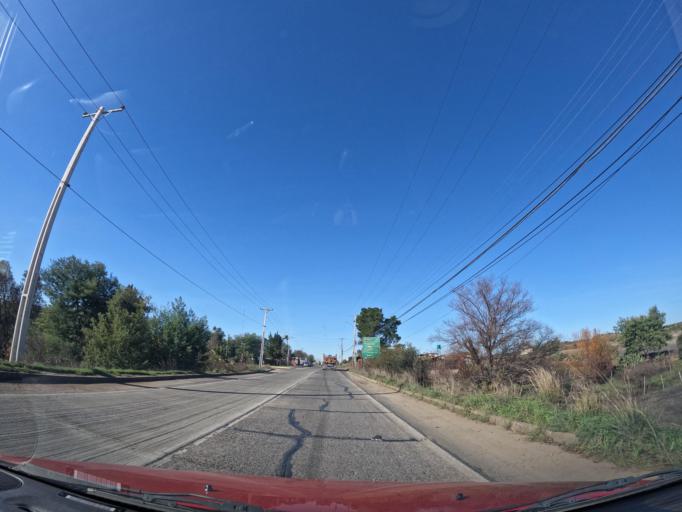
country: CL
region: Maule
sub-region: Provincia de Cauquenes
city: Cauquenes
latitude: -35.9577
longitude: -72.2755
